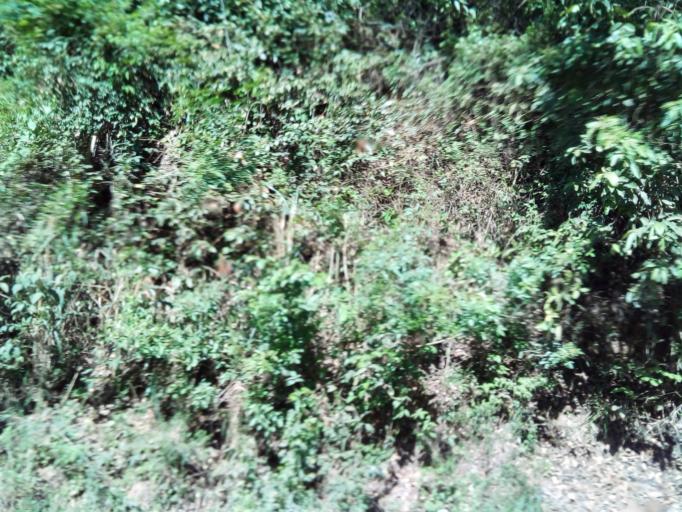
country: BR
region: Espirito Santo
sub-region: Vitoria
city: Vitoria
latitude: -20.2972
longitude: -40.3747
